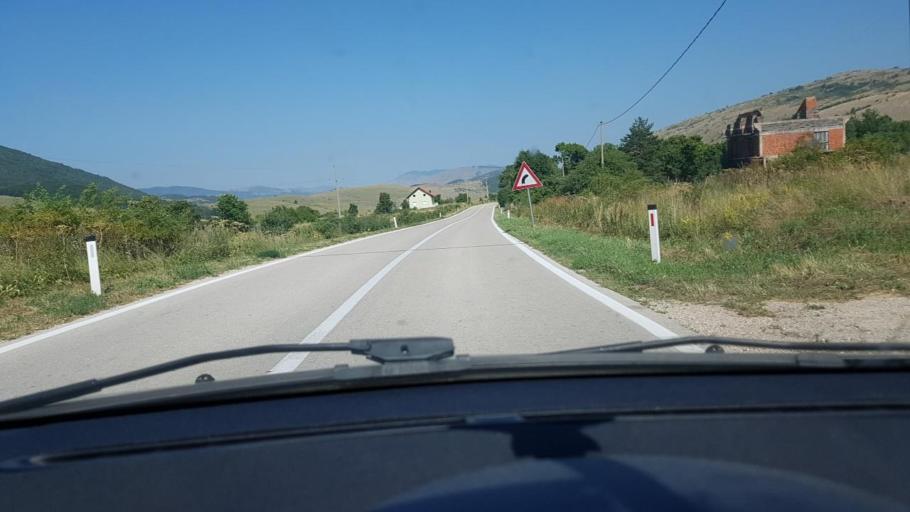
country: BA
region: Federation of Bosnia and Herzegovina
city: Bosansko Grahovo
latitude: 44.1208
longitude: 16.5329
